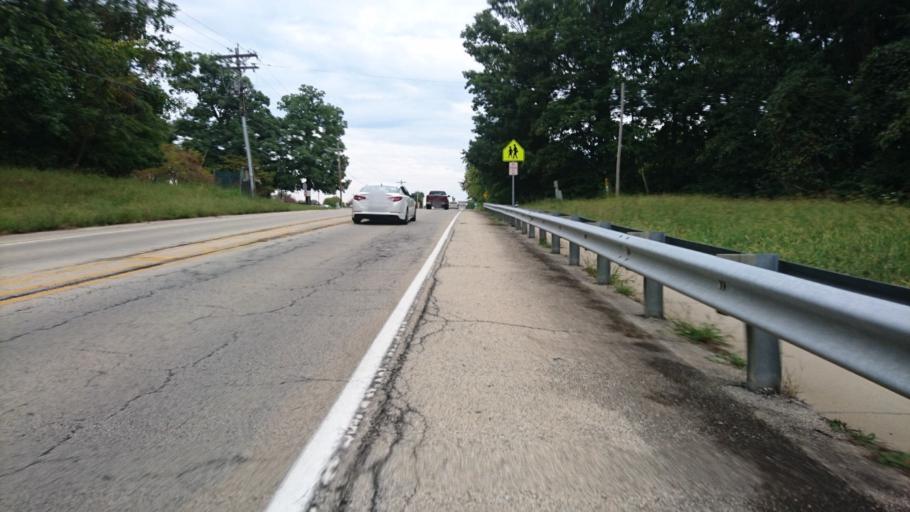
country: US
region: Illinois
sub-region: Sangamon County
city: Chatham
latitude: 39.6733
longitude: -89.6618
